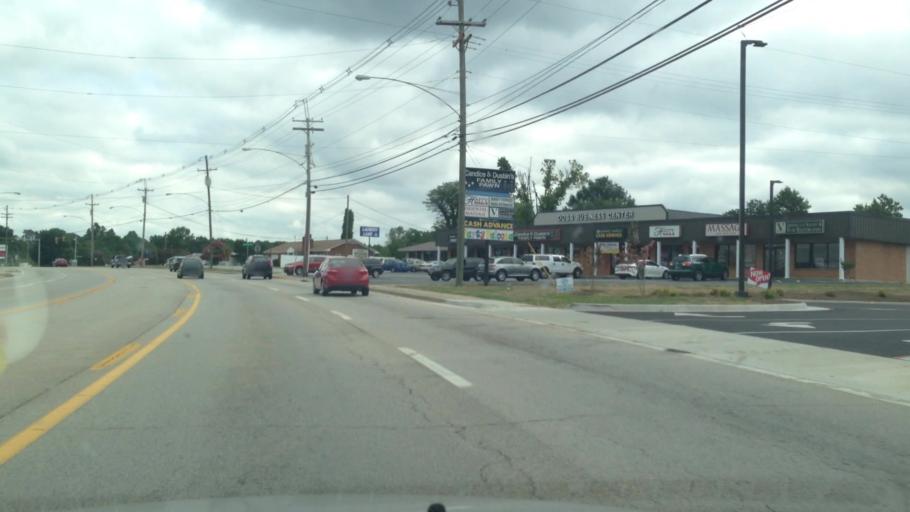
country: US
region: Virginia
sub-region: City of Danville
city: Danville
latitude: 36.6097
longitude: -79.4067
